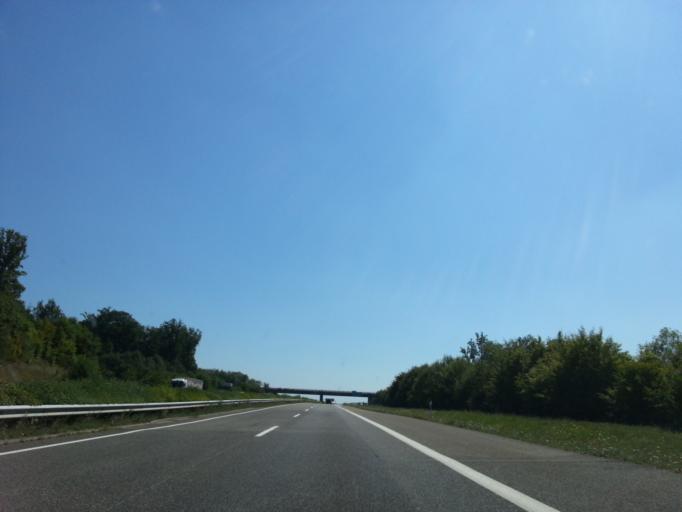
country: DE
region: Rheinland-Pfalz
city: Nattenheim
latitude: 50.0388
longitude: 6.5222
